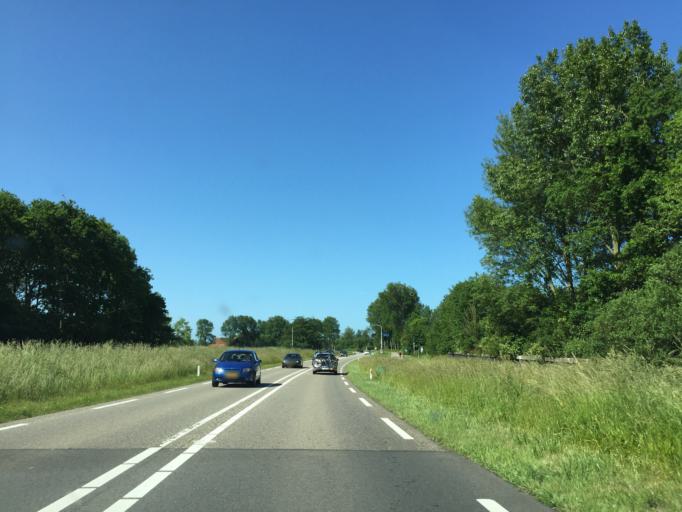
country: NL
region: Zeeland
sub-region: Schouwen-Duiveland
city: Burgh
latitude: 51.6889
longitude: 3.7400
